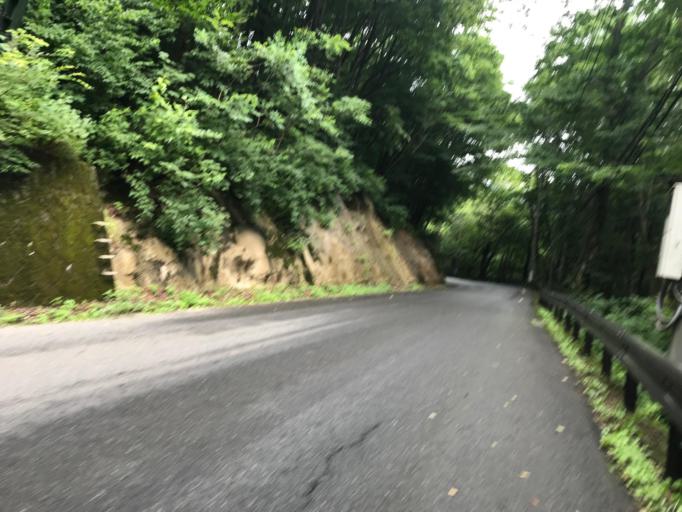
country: JP
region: Gunma
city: Numata
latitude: 36.8198
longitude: 138.9805
